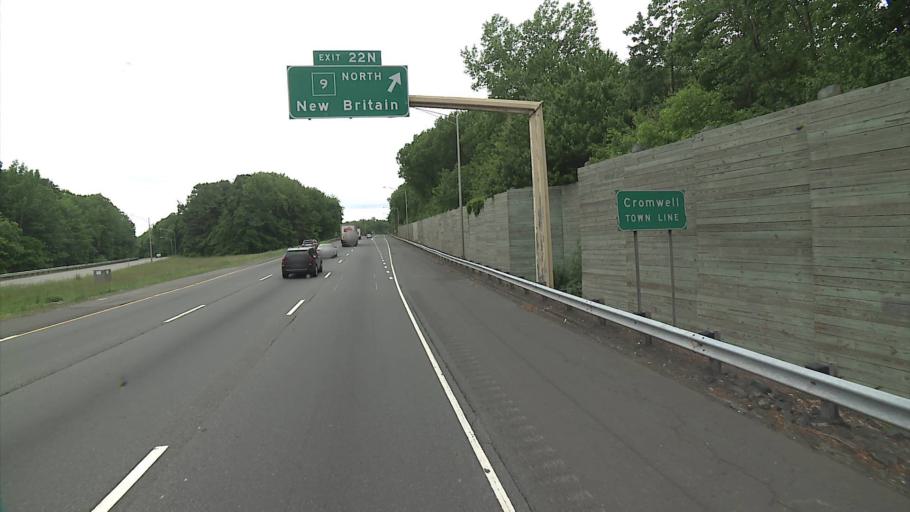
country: US
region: Connecticut
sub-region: Middlesex County
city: Cromwell
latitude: 41.6313
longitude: -72.6887
